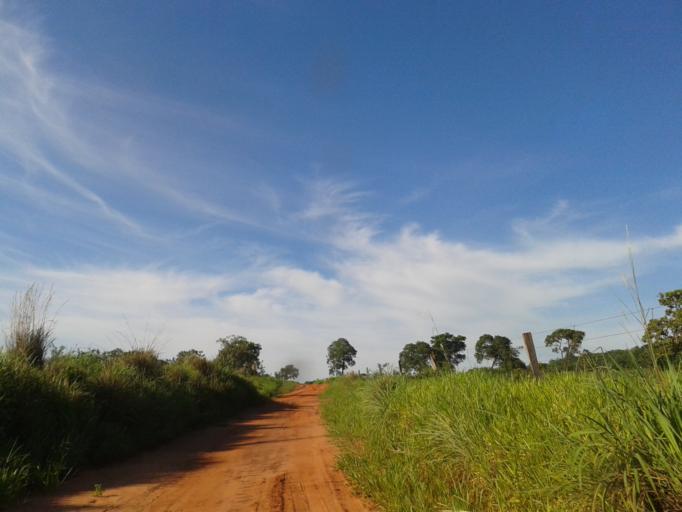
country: BR
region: Minas Gerais
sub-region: Santa Vitoria
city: Santa Vitoria
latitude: -19.0887
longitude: -49.9657
